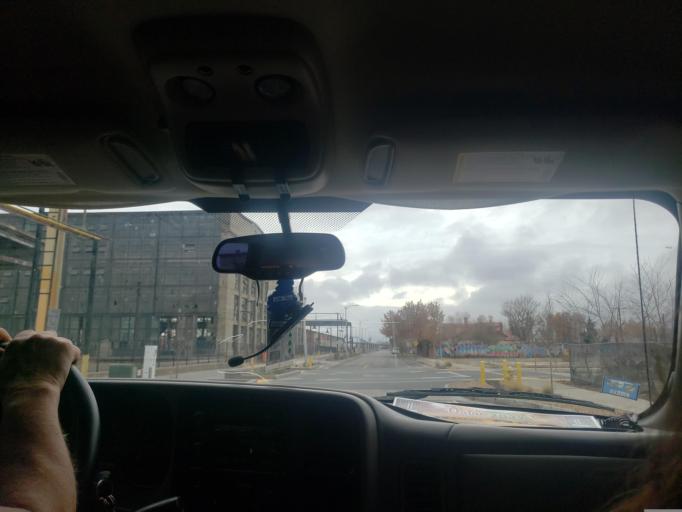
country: US
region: New Mexico
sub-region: Bernalillo County
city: Albuquerque
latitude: 35.0758
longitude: -106.6511
